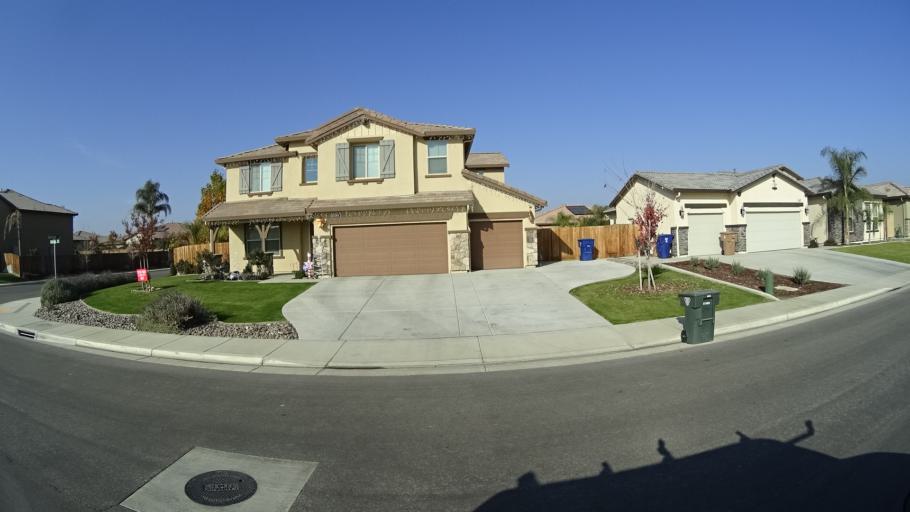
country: US
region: California
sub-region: Kern County
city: Rosedale
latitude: 35.3475
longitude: -119.1699
